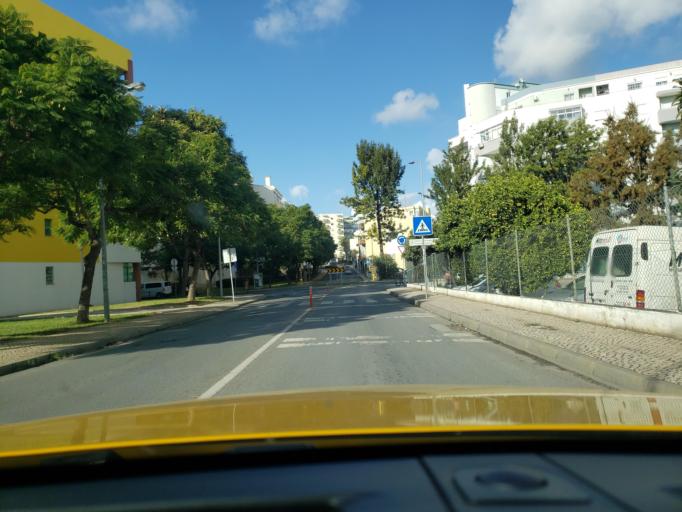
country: PT
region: Faro
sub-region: Portimao
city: Portimao
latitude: 37.1455
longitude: -8.5406
